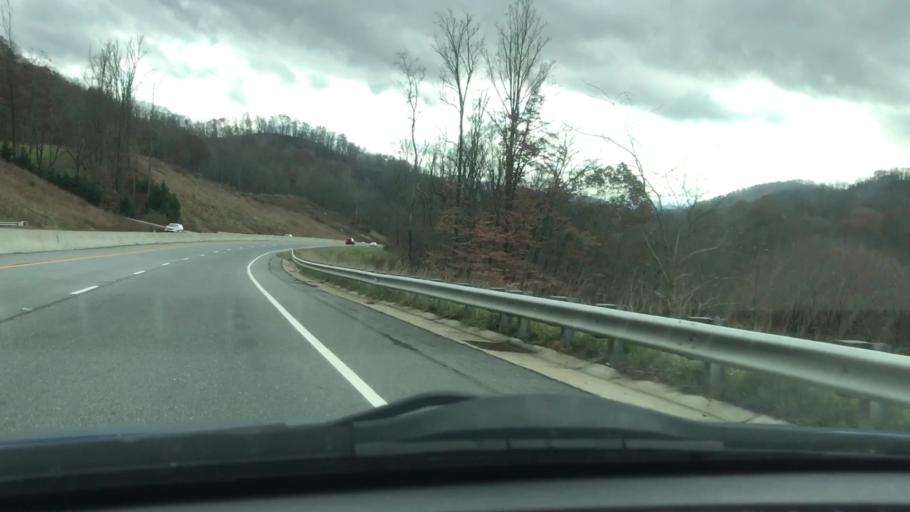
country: US
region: North Carolina
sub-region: Madison County
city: Mars Hill
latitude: 35.9001
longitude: -82.4725
